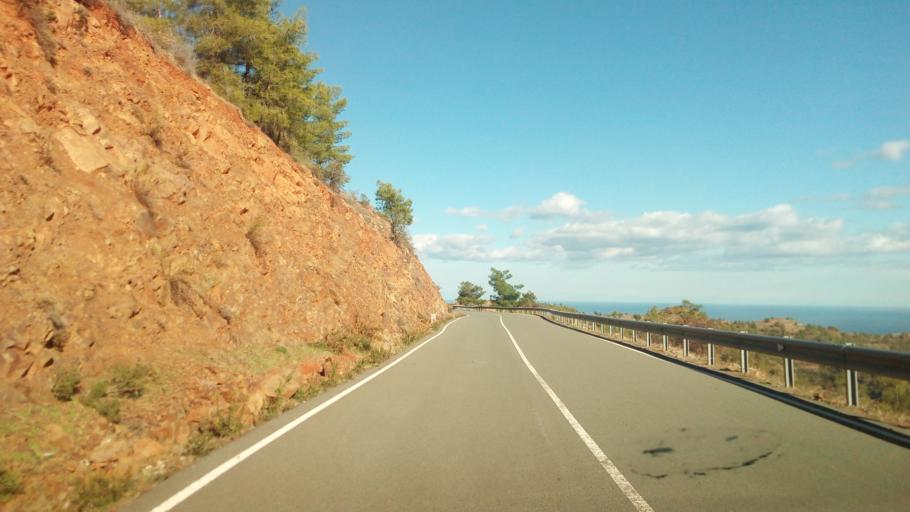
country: CY
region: Lefkosia
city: Lefka
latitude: 35.1032
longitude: 32.7570
